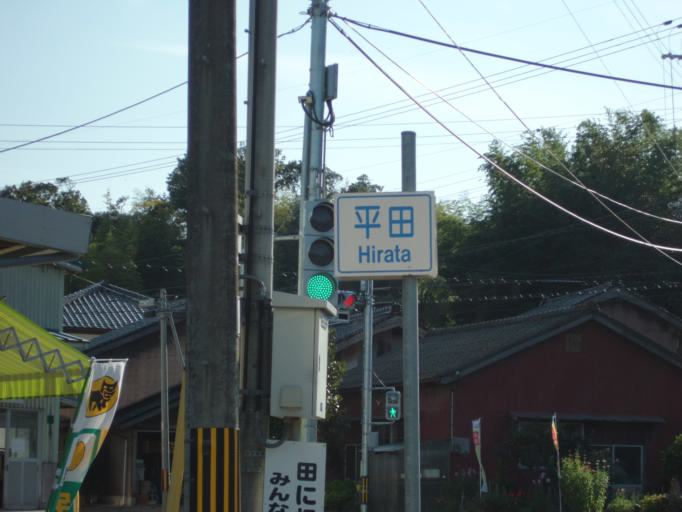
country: JP
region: Hyogo
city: Toyooka
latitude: 35.6362
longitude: 134.9416
